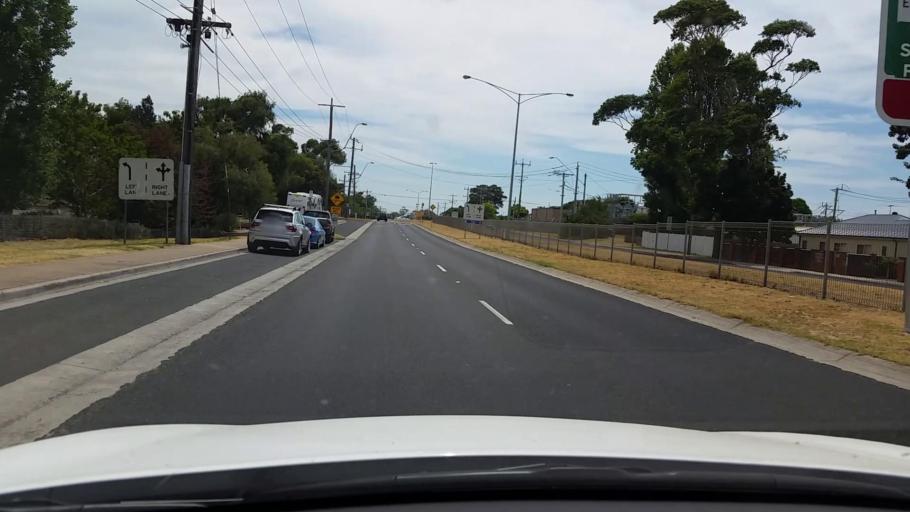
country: AU
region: Victoria
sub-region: Mornington Peninsula
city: Rosebud West
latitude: -38.3692
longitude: 144.8893
